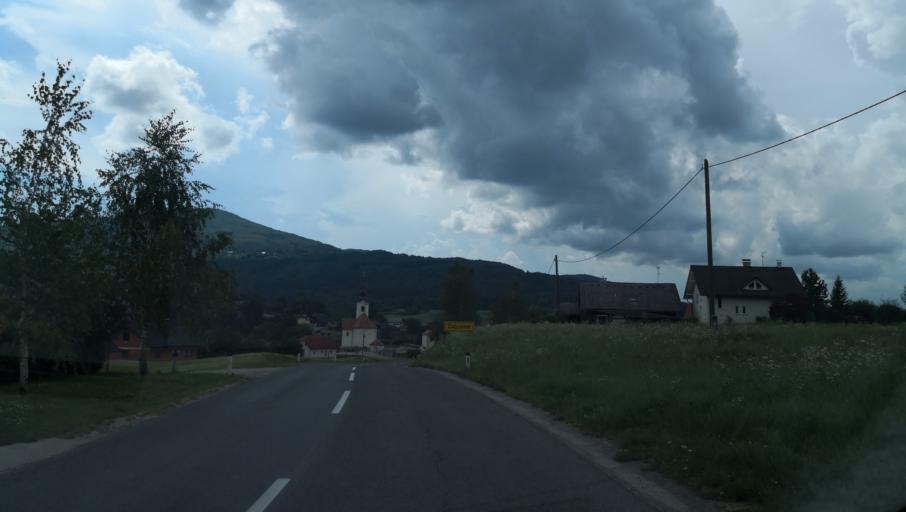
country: SI
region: Ivancna Gorica
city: Ivancna Gorica
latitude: 45.8584
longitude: 14.8398
